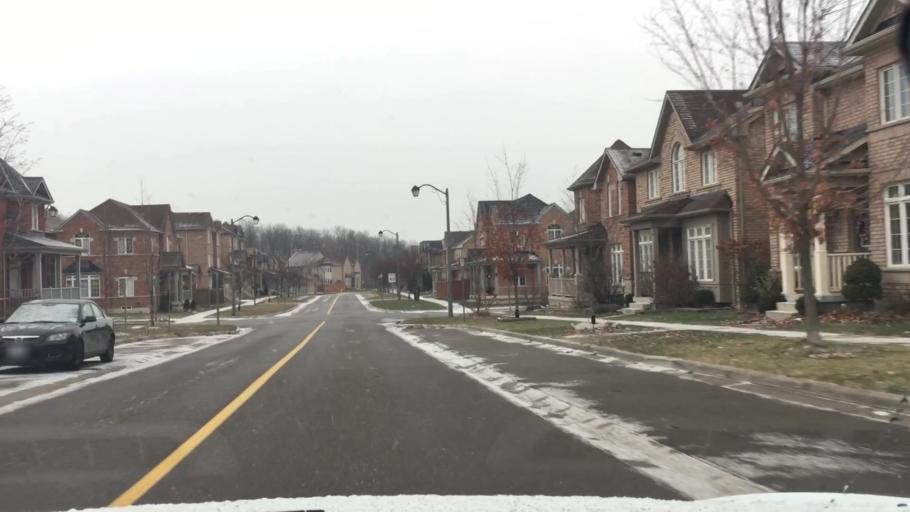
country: CA
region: Ontario
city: Markham
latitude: 43.8956
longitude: -79.2196
